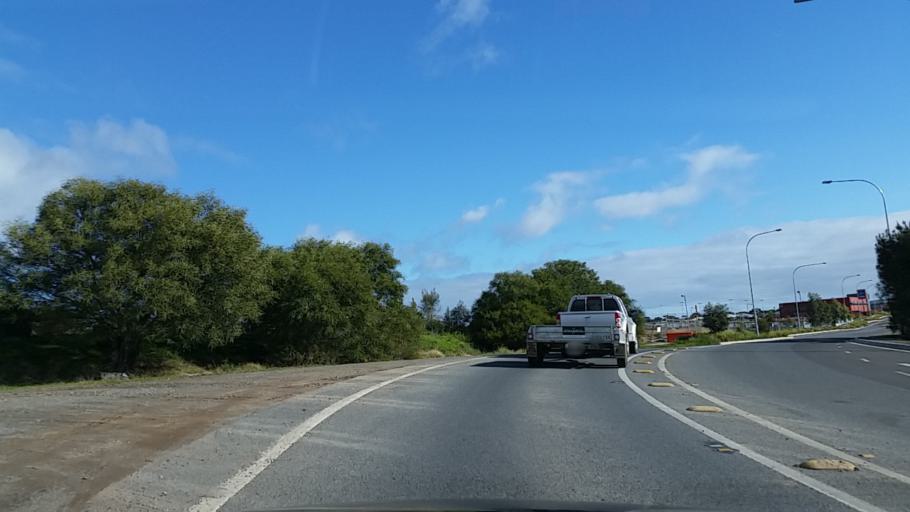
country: AU
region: South Australia
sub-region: Onkaparinga
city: Noarlunga
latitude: -35.1901
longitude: 138.4985
